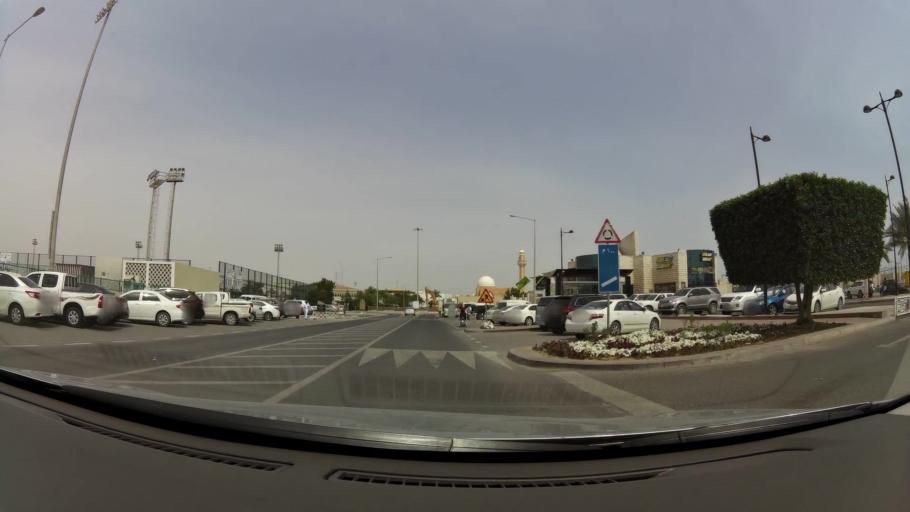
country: QA
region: Baladiyat ad Dawhah
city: Doha
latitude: 25.2671
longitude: 51.4821
